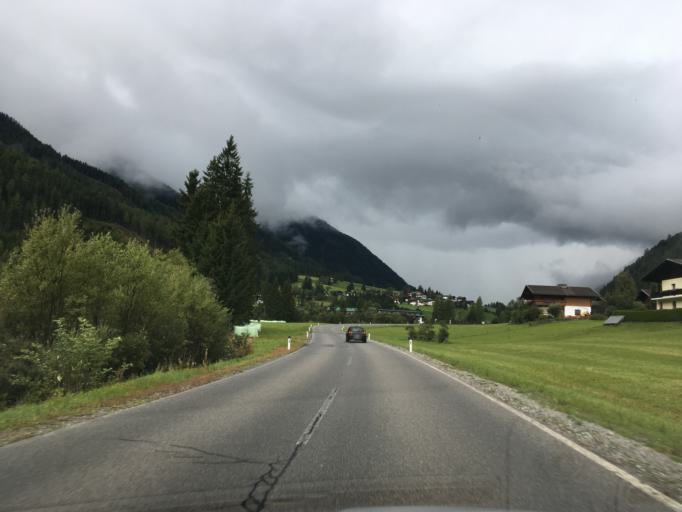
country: AT
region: Tyrol
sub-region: Politischer Bezirk Lienz
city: Innervillgraten
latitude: 46.9150
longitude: 12.3815
